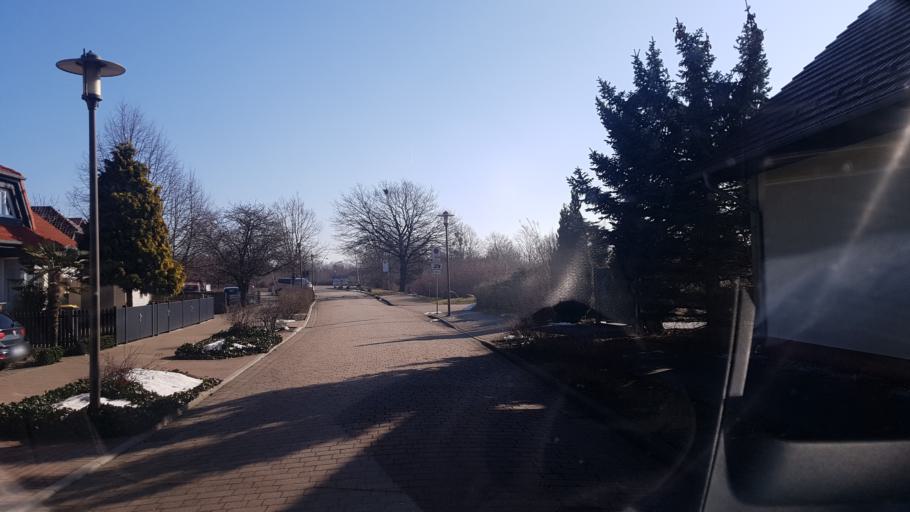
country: DE
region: Brandenburg
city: Senftenberg
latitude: 51.5127
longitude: 14.0223
